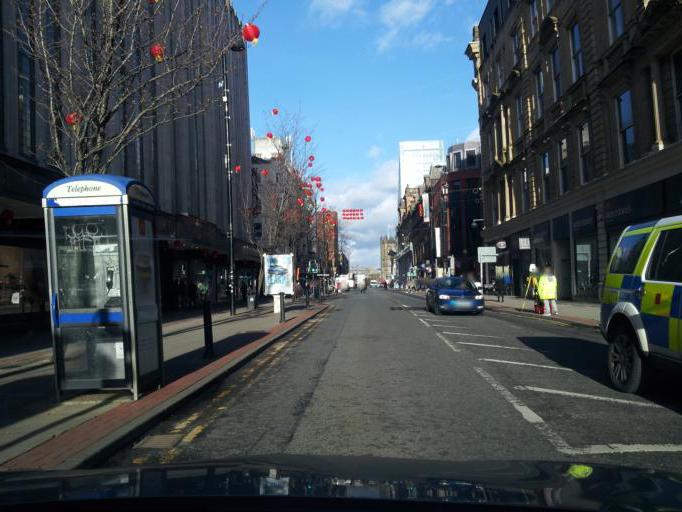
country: GB
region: England
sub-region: Manchester
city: Manchester
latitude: 53.4814
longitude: -2.2477
